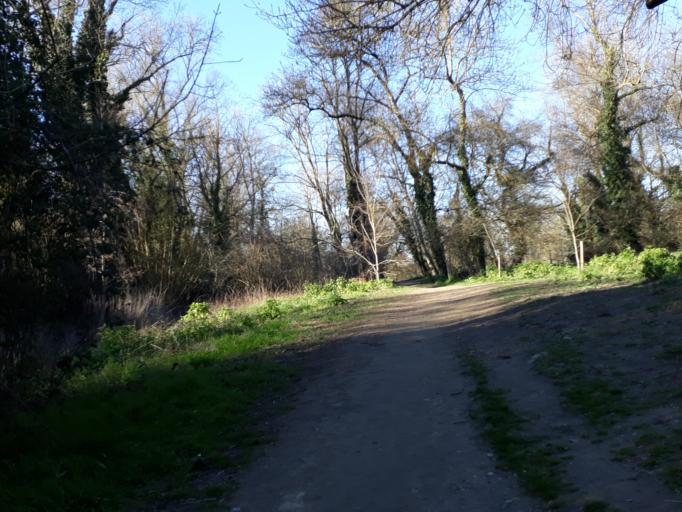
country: FR
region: Midi-Pyrenees
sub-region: Departement de la Haute-Garonne
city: Beauzelle
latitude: 43.6640
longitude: 1.3885
